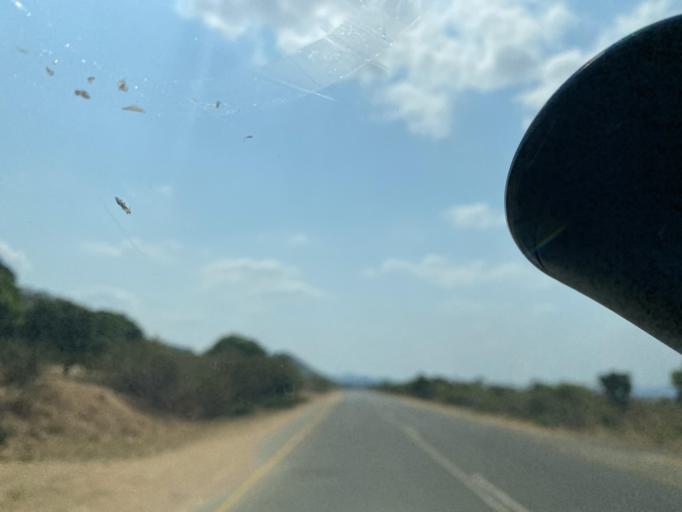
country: ZM
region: Lusaka
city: Chongwe
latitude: -15.6000
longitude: 28.7300
